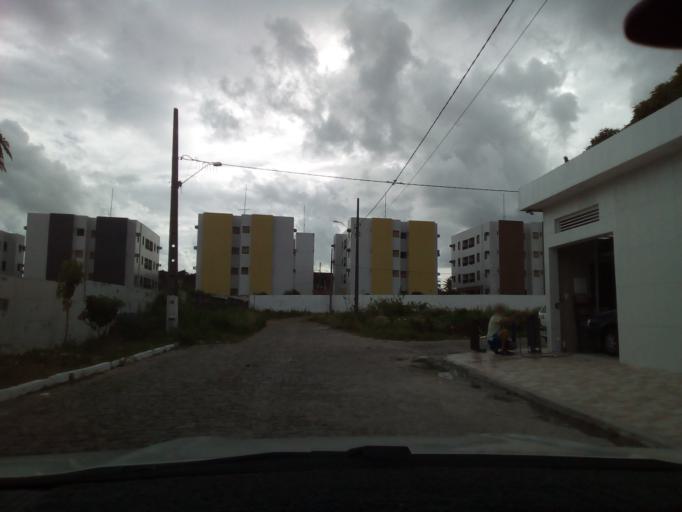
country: BR
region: Paraiba
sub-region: Joao Pessoa
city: Joao Pessoa
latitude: -7.1872
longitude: -34.8761
